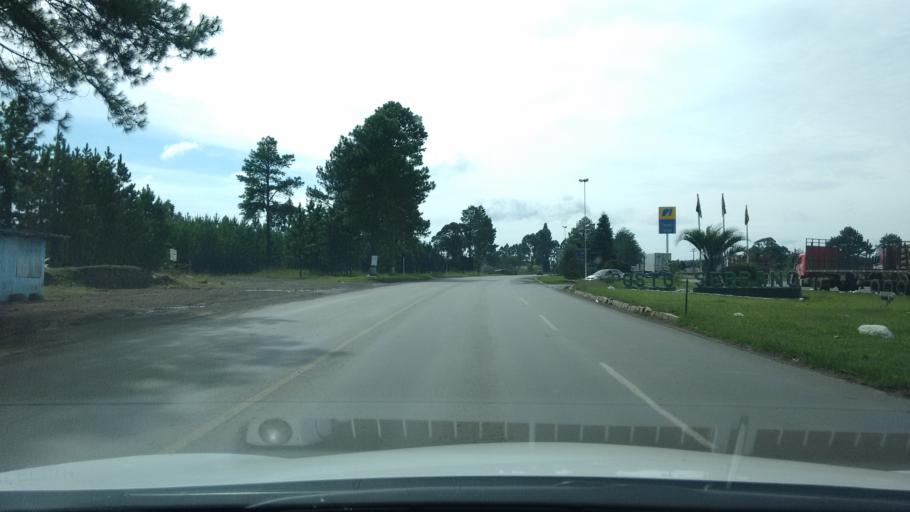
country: BR
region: Santa Catarina
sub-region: Curitibanos
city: Curitibanos
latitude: -27.3012
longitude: -50.4239
